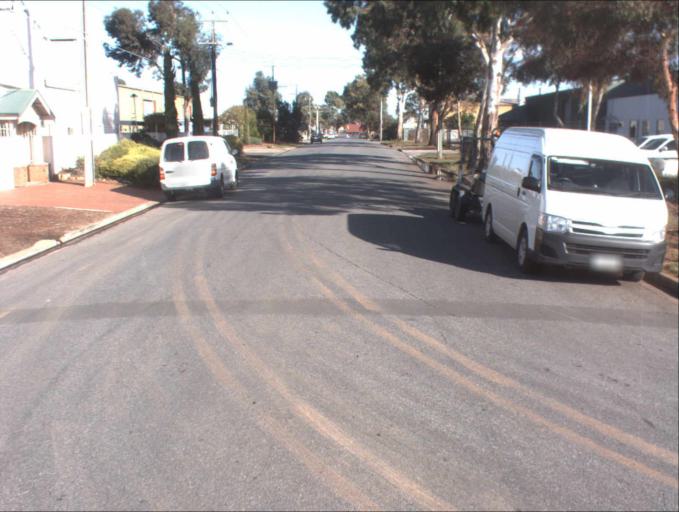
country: AU
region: South Australia
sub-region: Charles Sturt
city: Woodville North
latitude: -34.8458
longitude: 138.5495
